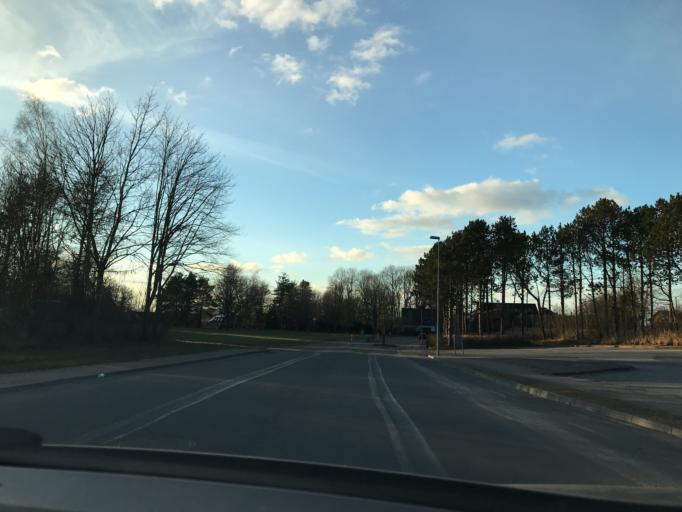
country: DK
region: South Denmark
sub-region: Middelfart Kommune
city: Norre Aby
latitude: 55.4540
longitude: 9.8705
